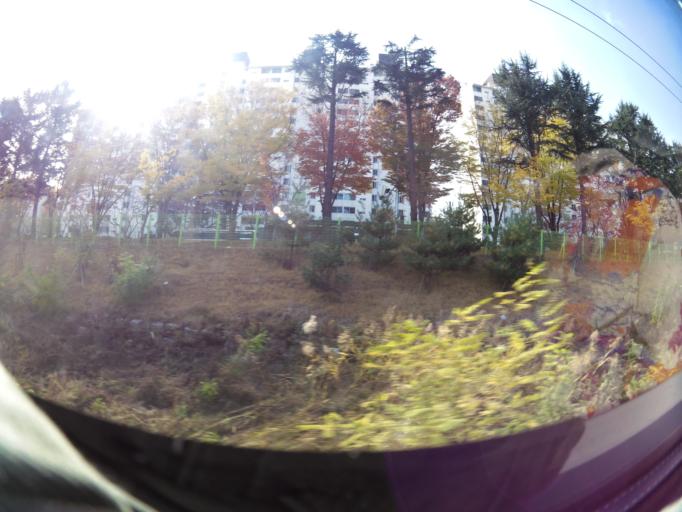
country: KR
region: Gyeongsangbuk-do
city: Gumi
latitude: 36.1227
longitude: 128.3452
